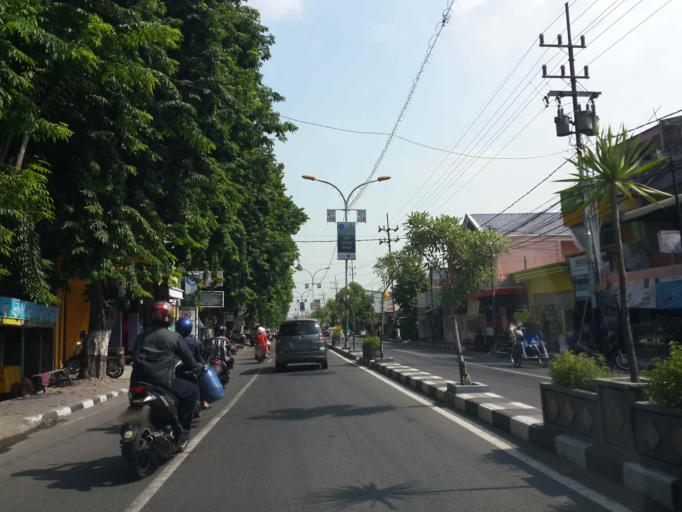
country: ID
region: East Java
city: Kebomas
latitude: -7.1747
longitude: 112.6521
